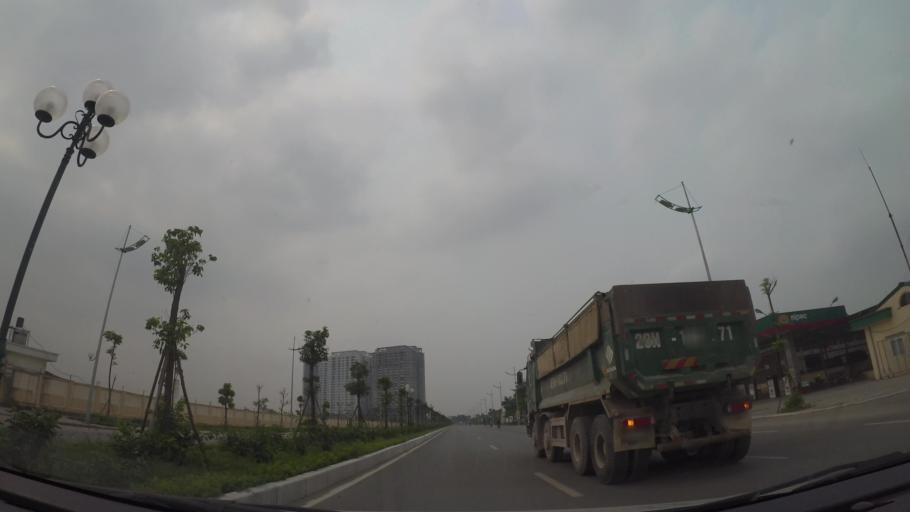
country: VN
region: Ha Noi
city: Cau Dien
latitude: 21.0437
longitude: 105.7374
